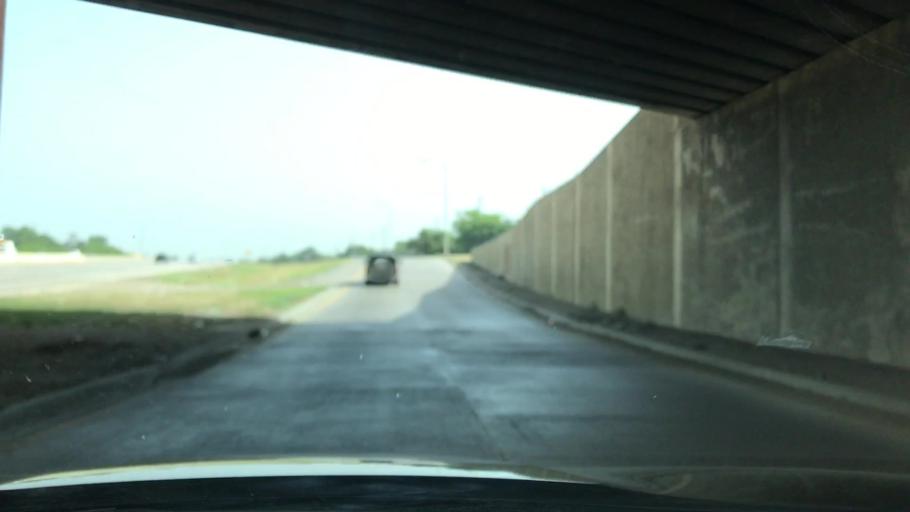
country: US
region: Texas
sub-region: Dallas County
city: Cockrell Hill
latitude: 32.7664
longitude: -96.9144
